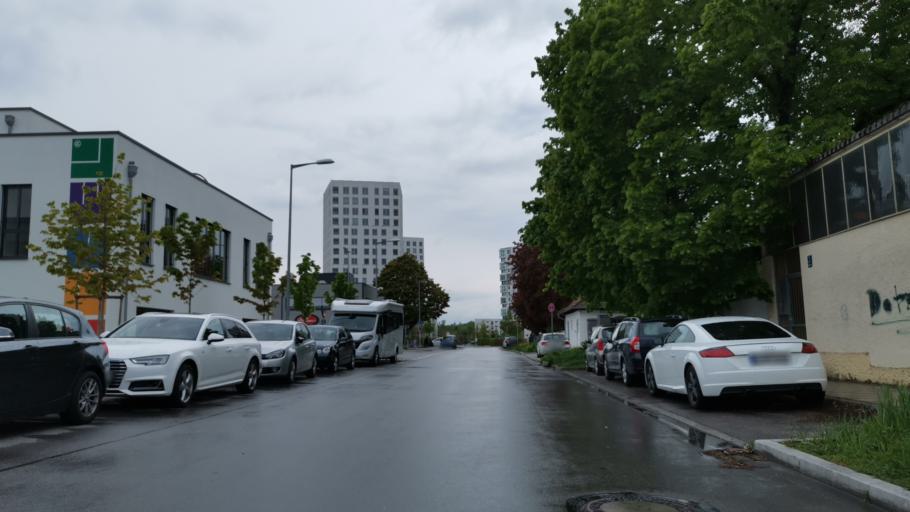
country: DE
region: Bavaria
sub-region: Upper Bavaria
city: Pullach im Isartal
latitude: 48.0947
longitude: 11.5347
